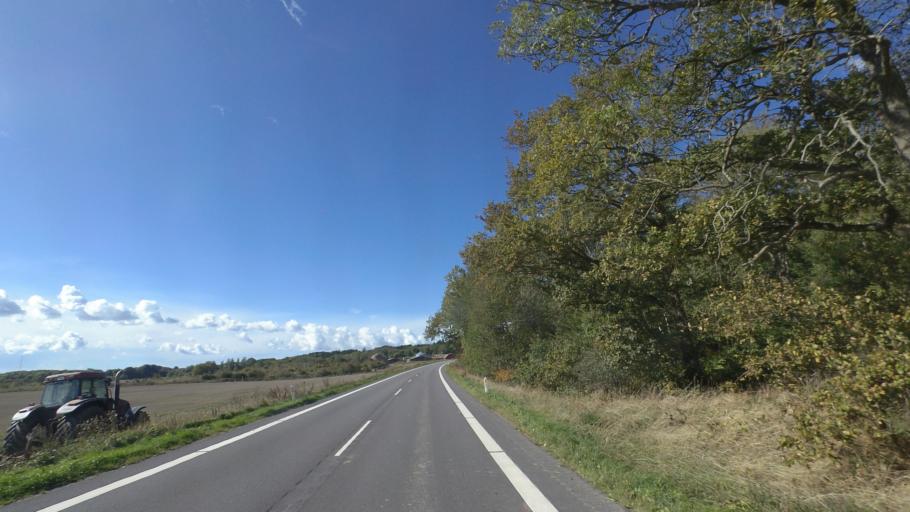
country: DK
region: Capital Region
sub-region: Bornholm Kommune
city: Nexo
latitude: 55.0628
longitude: 15.0284
